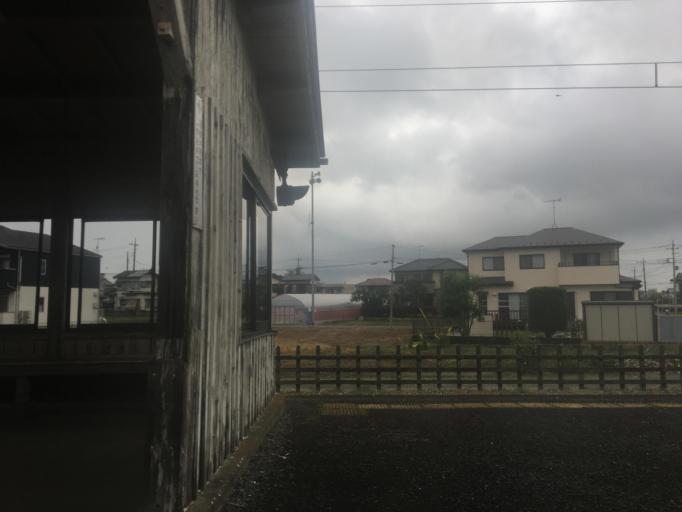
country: JP
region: Saitama
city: Yorii
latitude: 36.1353
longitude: 139.2595
